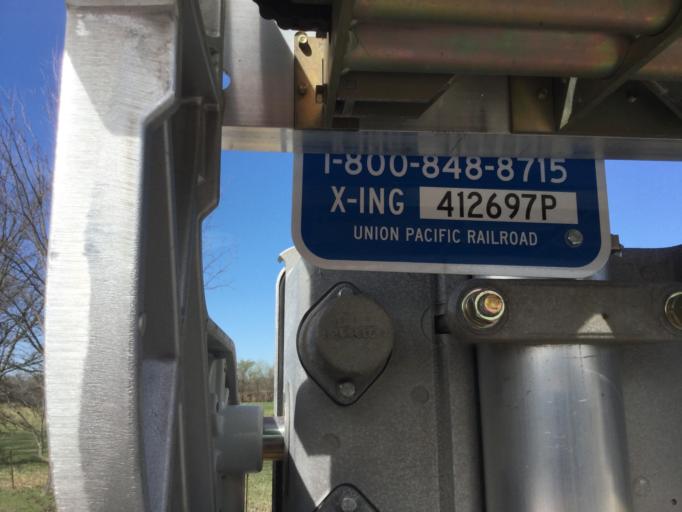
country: US
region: Kansas
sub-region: Neosho County
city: Erie
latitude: 37.6470
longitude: -95.1791
